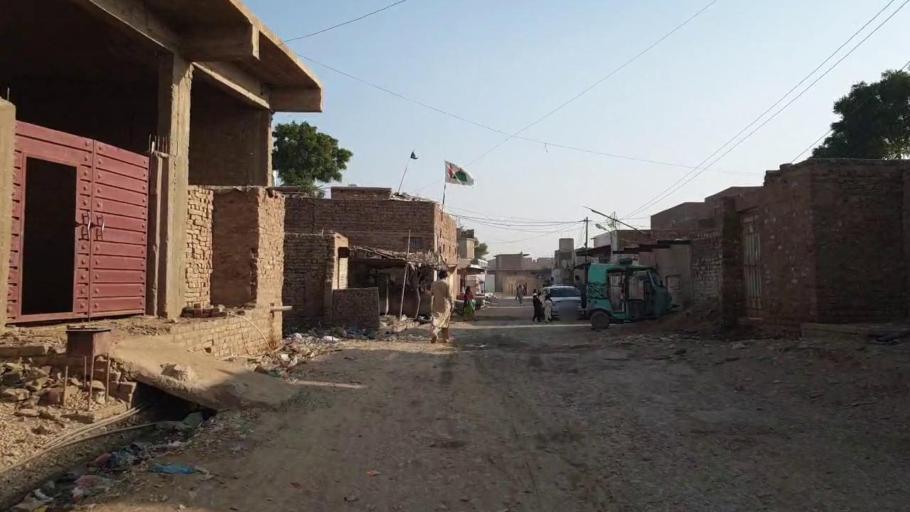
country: PK
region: Sindh
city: Kotri
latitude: 25.3556
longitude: 68.2640
